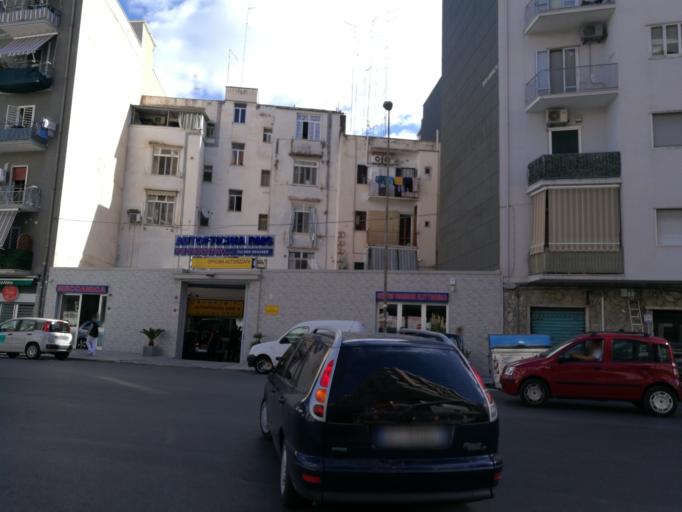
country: IT
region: Apulia
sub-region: Provincia di Bari
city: Bari
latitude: 41.1230
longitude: 16.8518
